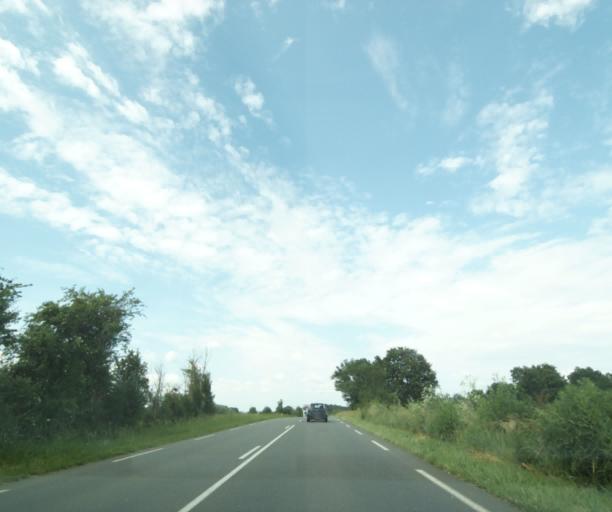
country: FR
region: Pays de la Loire
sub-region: Departement de Maine-et-Loire
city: Montreuil-Bellay
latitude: 47.1725
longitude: -0.1376
